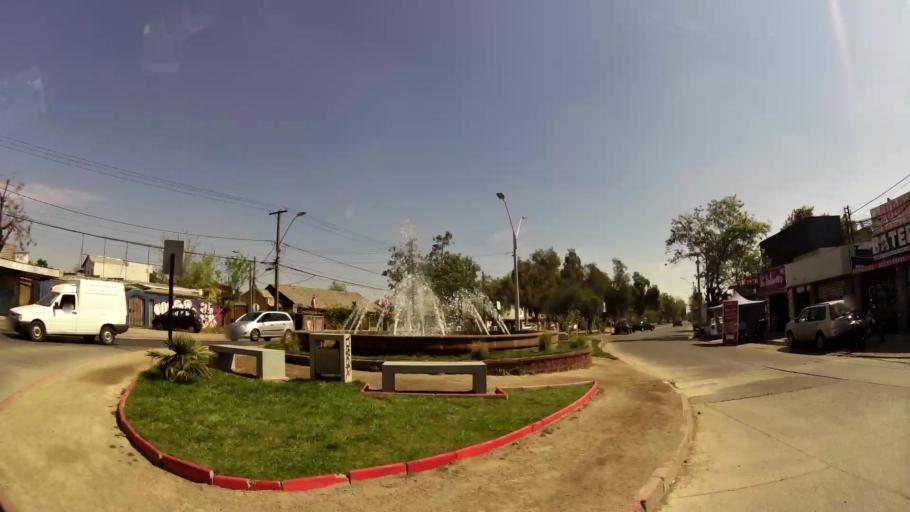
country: CL
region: Santiago Metropolitan
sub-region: Provincia de Santiago
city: La Pintana
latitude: -33.5282
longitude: -70.6359
